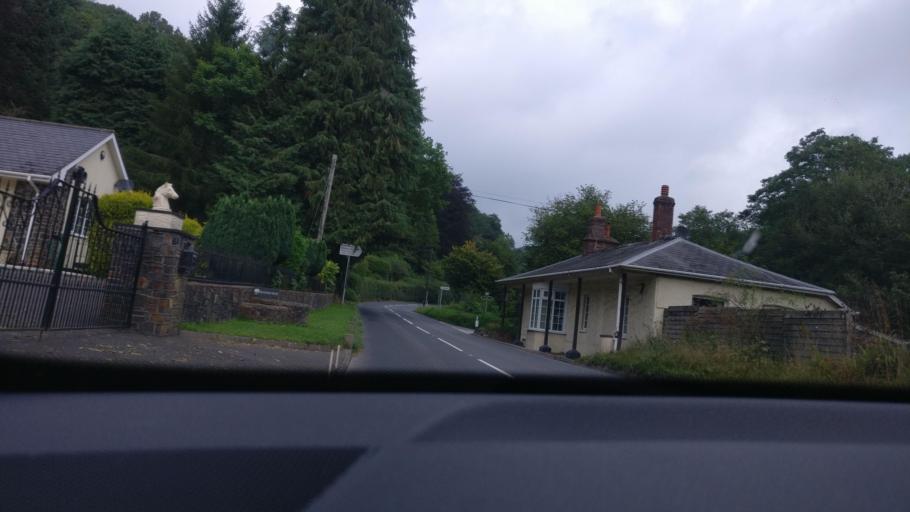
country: GB
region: England
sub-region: Devon
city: South Molton
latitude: 51.0765
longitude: -3.8669
